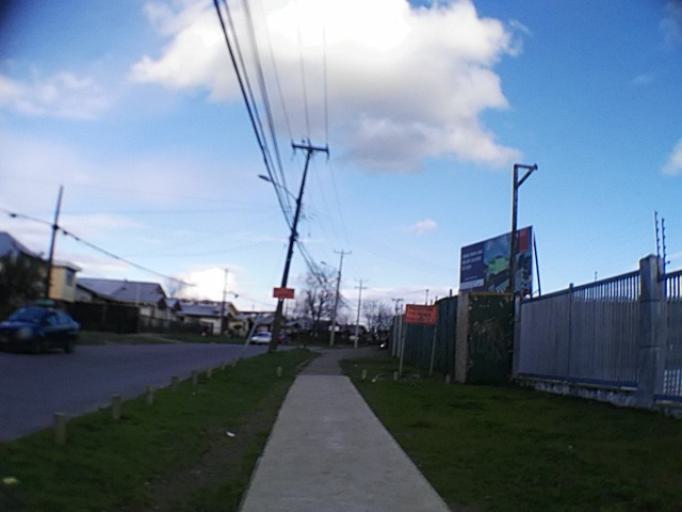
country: CL
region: Los Lagos
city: Las Animas
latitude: -39.8370
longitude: -73.2192
